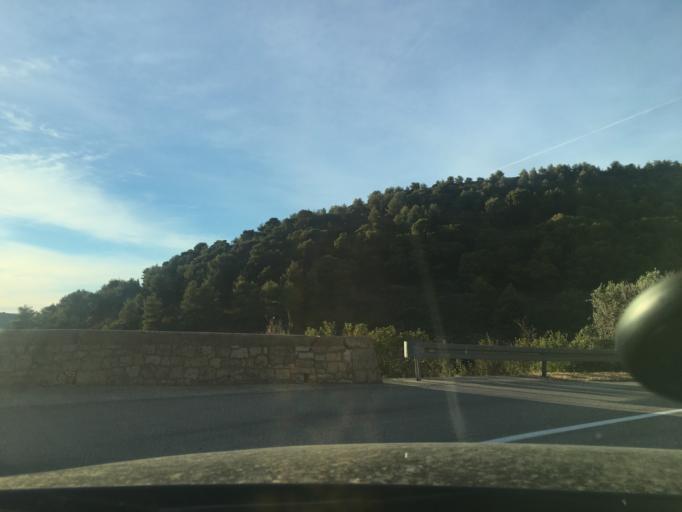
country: HR
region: Splitsko-Dalmatinska
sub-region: Grad Vis
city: Vis
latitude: 43.0573
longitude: 16.2039
